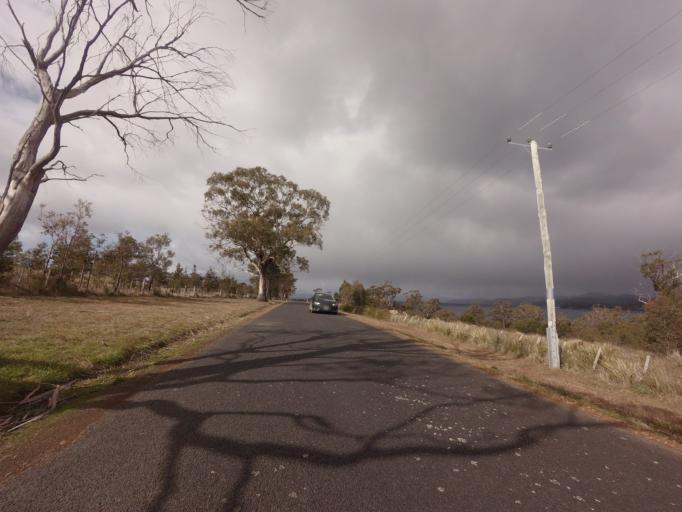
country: AU
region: Tasmania
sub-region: Sorell
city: Sorell
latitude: -42.5417
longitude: 147.9020
